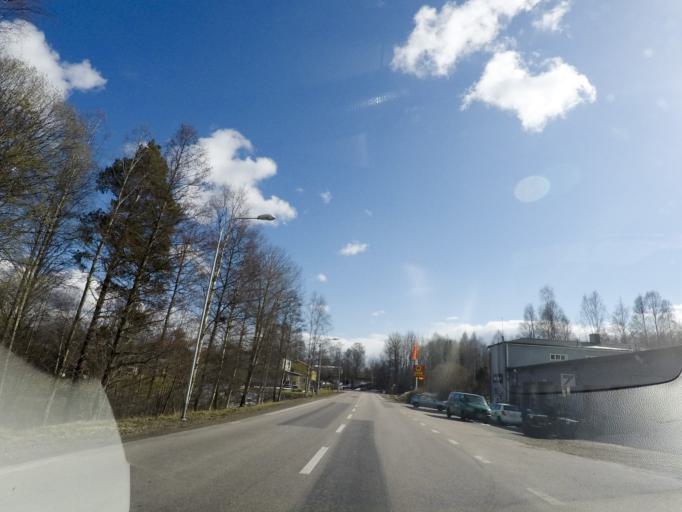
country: SE
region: Vaestmanland
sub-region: Skinnskattebergs Kommun
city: Skinnskatteberg
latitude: 59.8318
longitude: 15.6766
